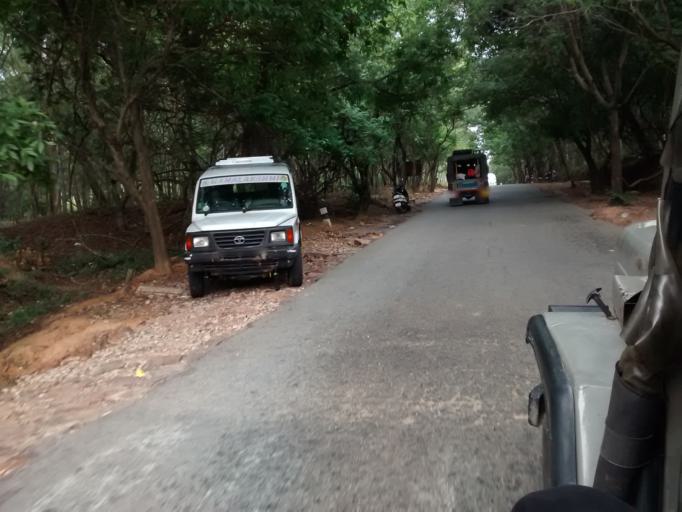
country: IN
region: Andhra Pradesh
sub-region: Chittoor
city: Tirumala
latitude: 13.7039
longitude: 79.3453
